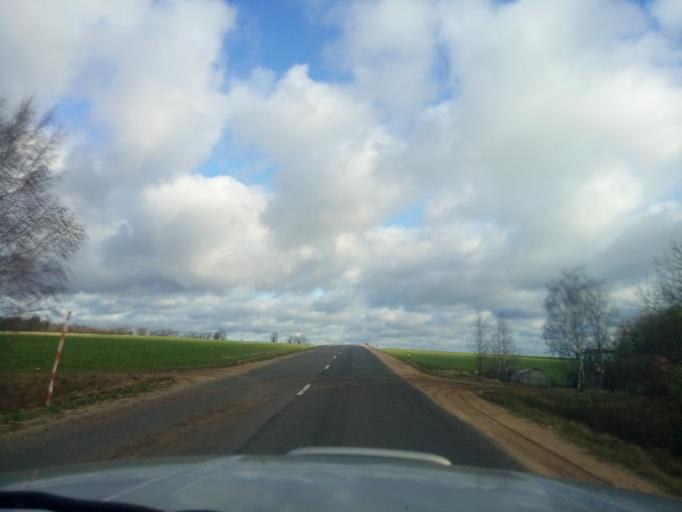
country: BY
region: Minsk
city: Kapyl'
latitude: 53.1451
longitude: 27.0383
